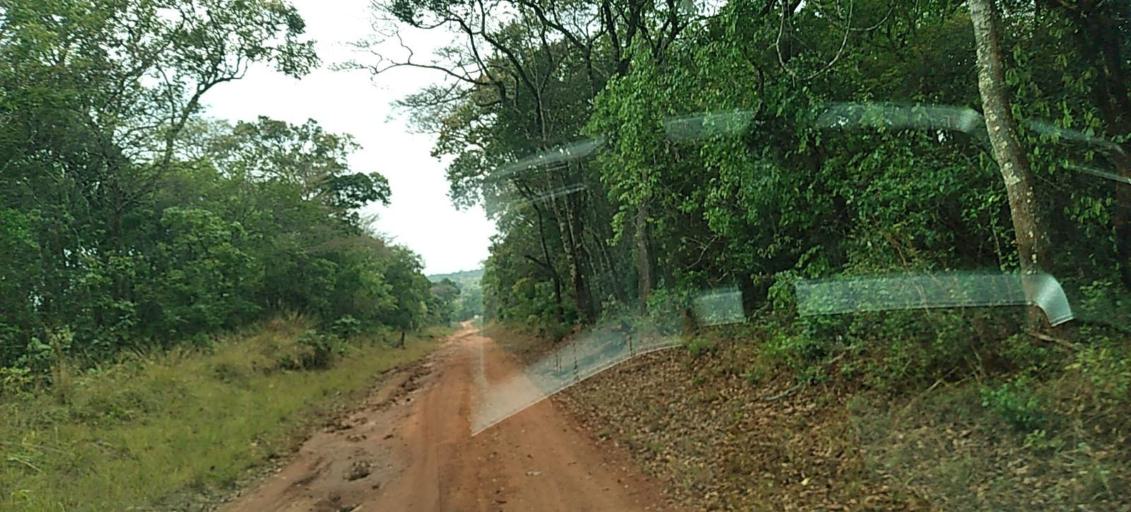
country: ZM
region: North-Western
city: Mwinilunga
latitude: -11.5411
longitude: 24.7810
